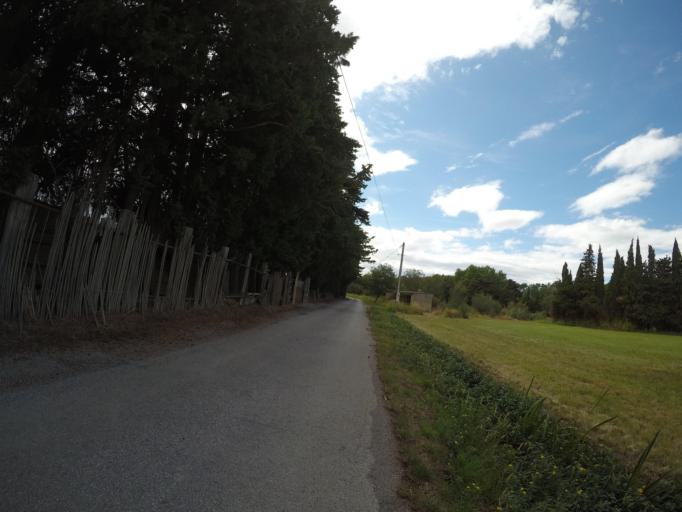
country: FR
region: Languedoc-Roussillon
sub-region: Departement des Pyrenees-Orientales
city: Pezilla-la-Riviere
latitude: 42.7003
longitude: 2.7827
